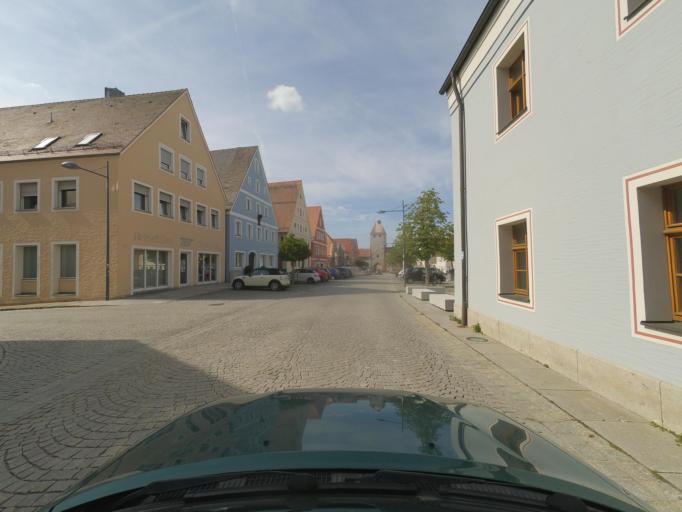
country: DE
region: Bavaria
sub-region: Upper Palatinate
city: Freystadt
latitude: 49.1990
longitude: 11.3284
